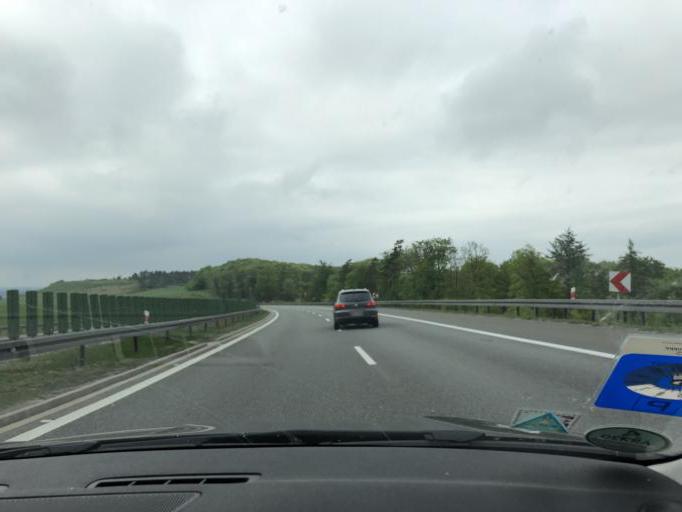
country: PL
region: Opole Voivodeship
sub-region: Powiat krapkowicki
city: Zdzieszowice
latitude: 50.4766
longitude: 18.1365
